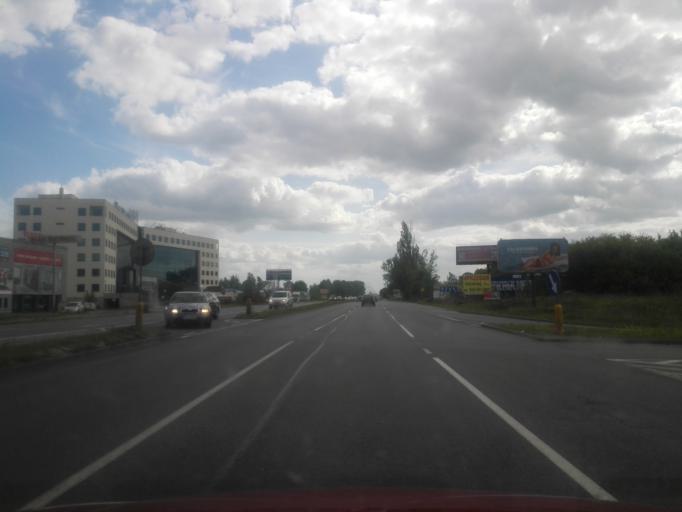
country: PL
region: Masovian Voivodeship
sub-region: Powiat wolominski
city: Zabki
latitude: 52.3019
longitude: 21.0876
